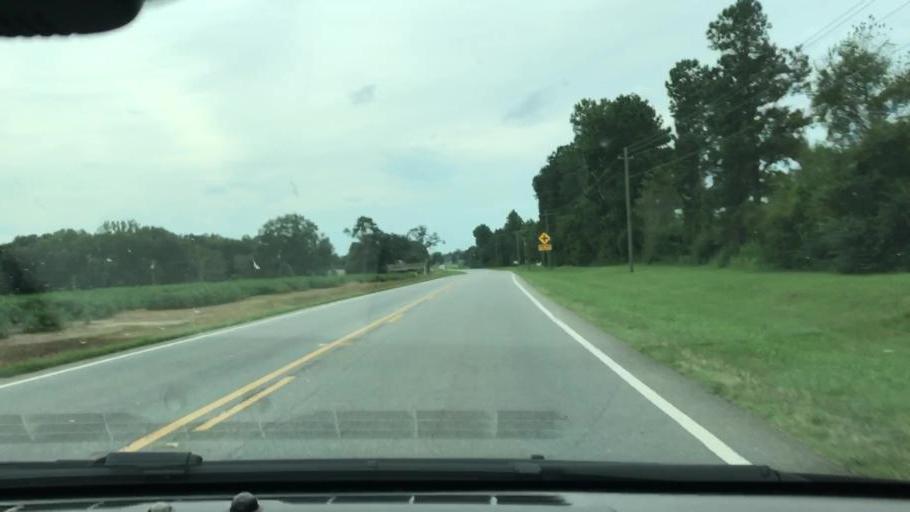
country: US
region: Georgia
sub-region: Early County
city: Blakely
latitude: 31.3848
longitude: -84.9574
